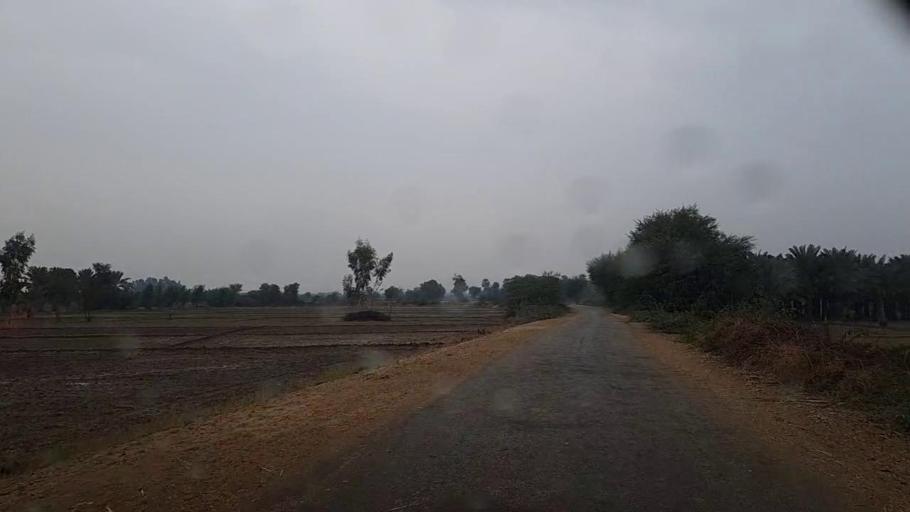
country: PK
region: Sindh
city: Ranipur
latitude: 27.2607
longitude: 68.5755
